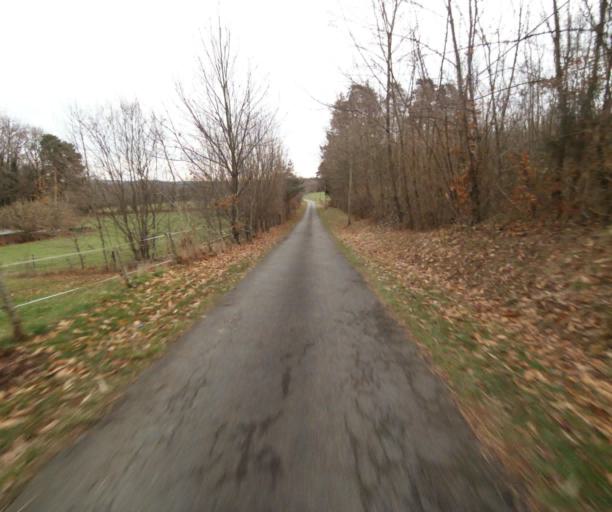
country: FR
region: Limousin
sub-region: Departement de la Correze
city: Chameyrat
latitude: 45.2325
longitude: 1.6716
